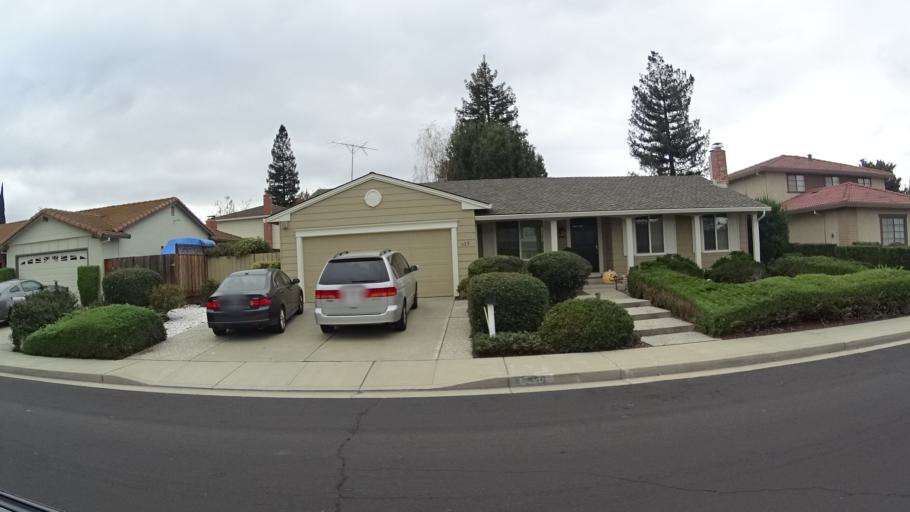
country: US
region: California
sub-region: Santa Clara County
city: Santa Clara
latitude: 37.3288
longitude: -121.9703
